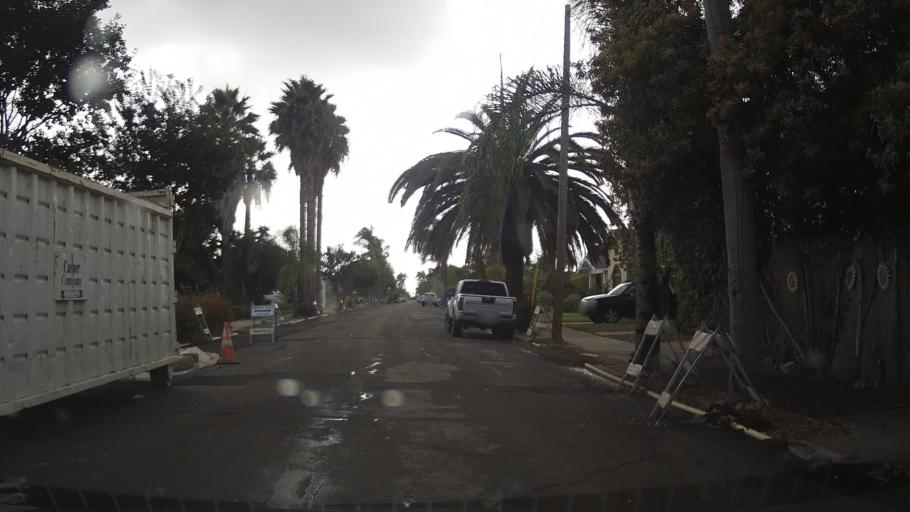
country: US
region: California
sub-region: San Diego County
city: San Diego
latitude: 32.7392
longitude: -117.1221
